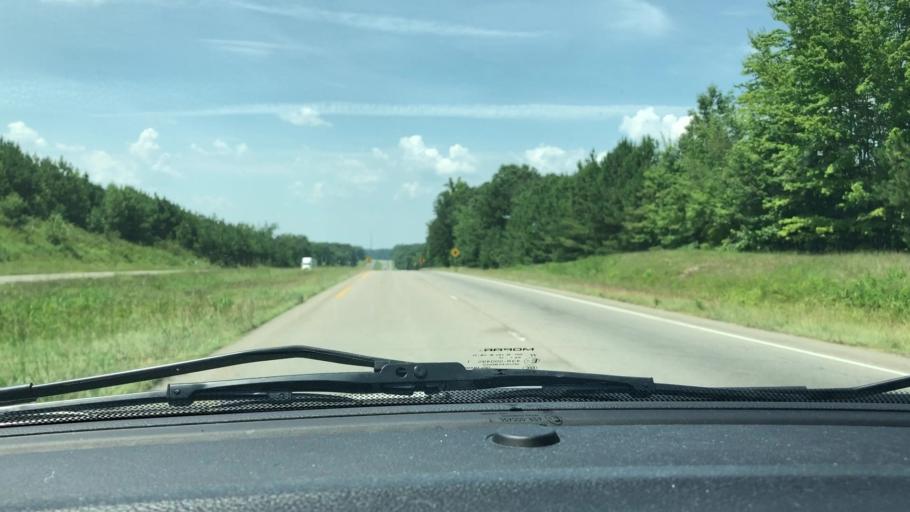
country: US
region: North Carolina
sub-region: Chatham County
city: Siler City
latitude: 35.6281
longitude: -79.3653
